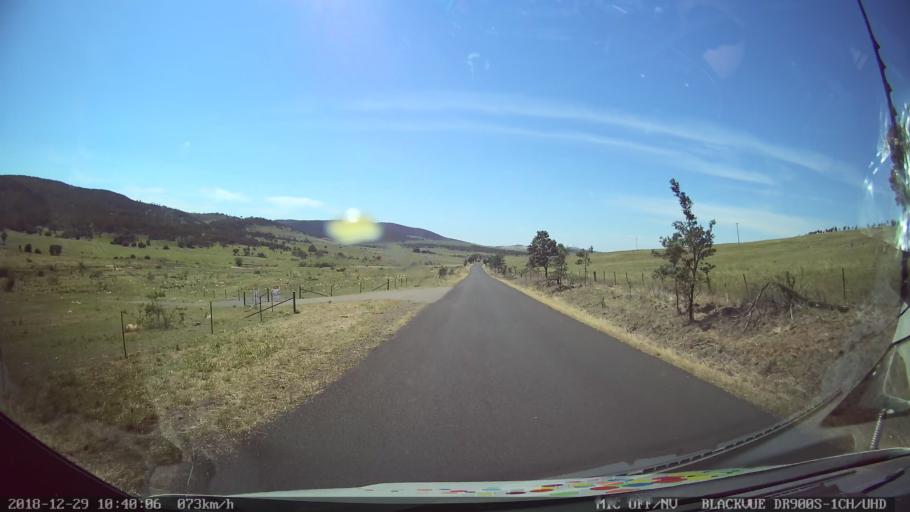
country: AU
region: New South Wales
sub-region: Palerang
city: Bungendore
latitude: -35.0126
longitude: 149.5153
